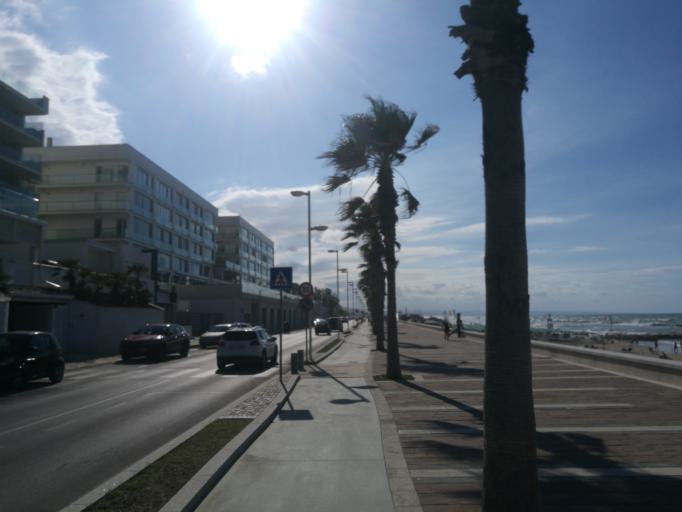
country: IT
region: Molise
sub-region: Provincia di Campobasso
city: Termoli
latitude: 42.0059
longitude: 14.9831
